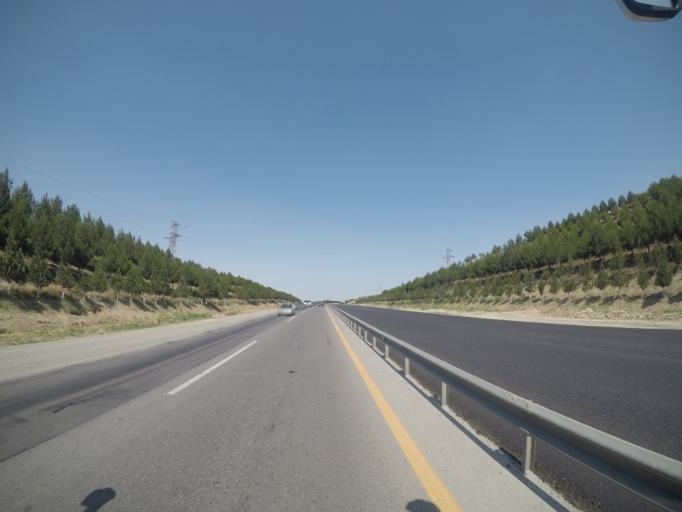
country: AZ
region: Haciqabul
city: Haciqabul
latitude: 40.0460
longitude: 48.9787
